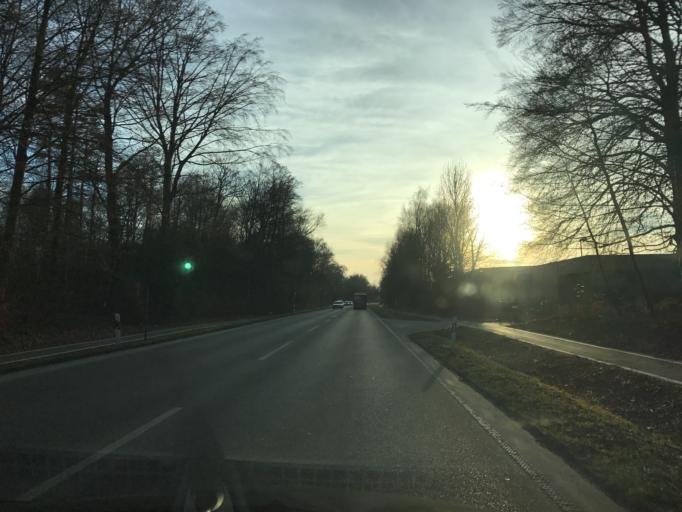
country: DE
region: Baden-Wuerttemberg
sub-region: Tuebingen Region
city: Friedrichshafen
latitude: 47.6641
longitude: 9.5100
